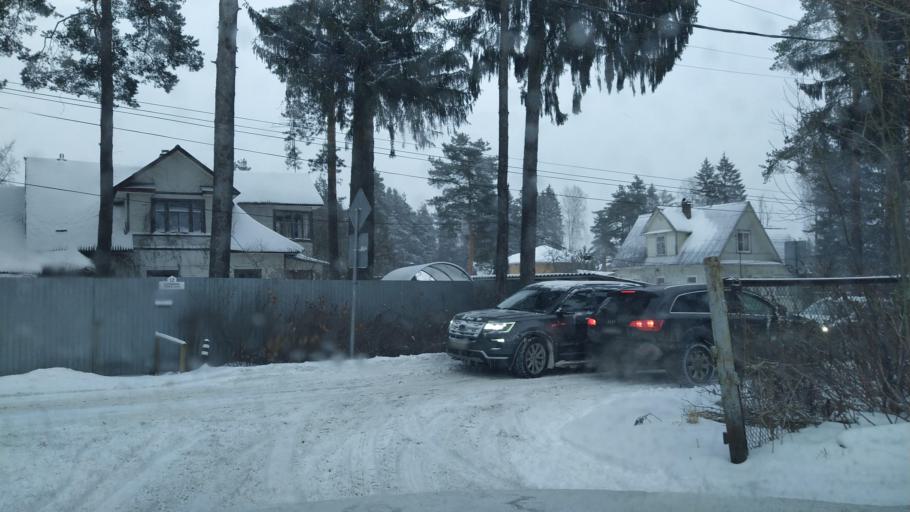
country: RU
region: Leningrad
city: Vsevolozhsk
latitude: 60.0247
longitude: 30.6823
